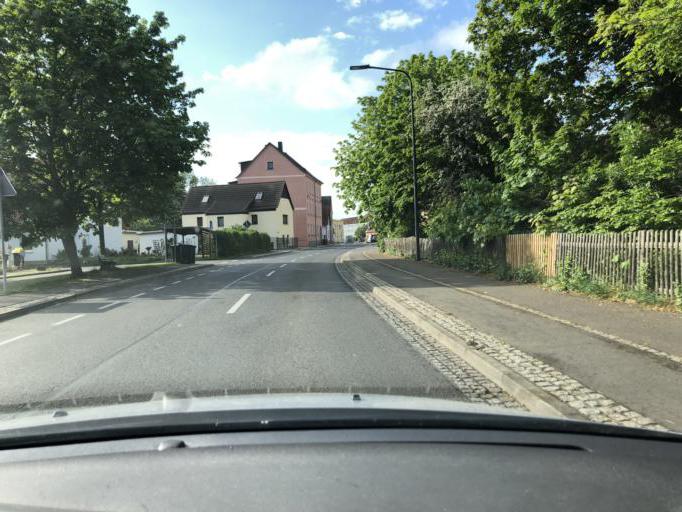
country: DE
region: Saxony
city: Markkleeberg
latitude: 51.2612
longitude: 12.3782
